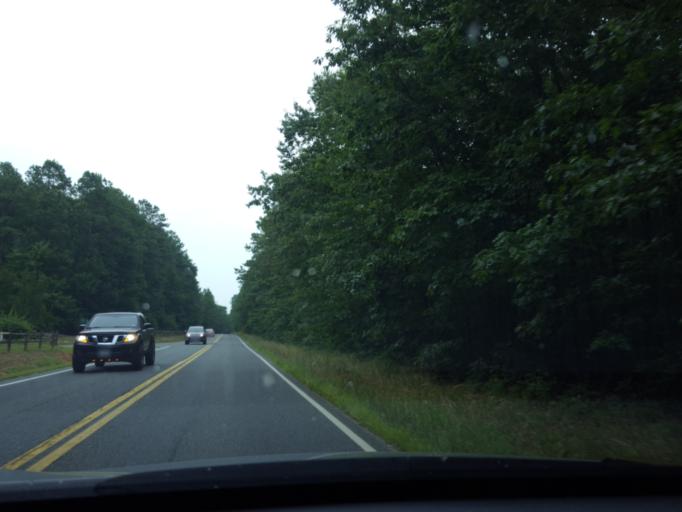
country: US
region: Virginia
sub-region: Spotsylvania County
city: Spotsylvania
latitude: 38.3042
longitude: -77.6909
